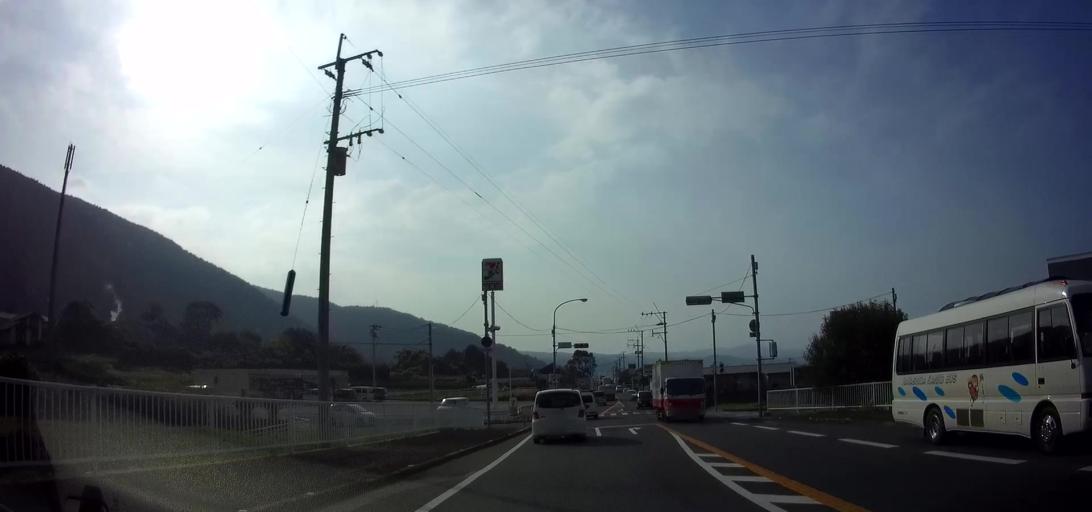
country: JP
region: Nagasaki
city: Shimabara
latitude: 32.7515
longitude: 130.2112
